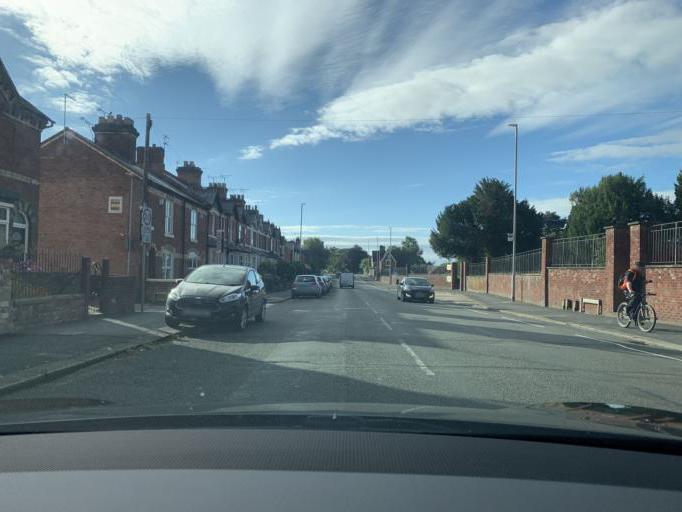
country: GB
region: England
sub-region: Staffordshire
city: Stafford
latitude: 52.8177
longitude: -2.1289
